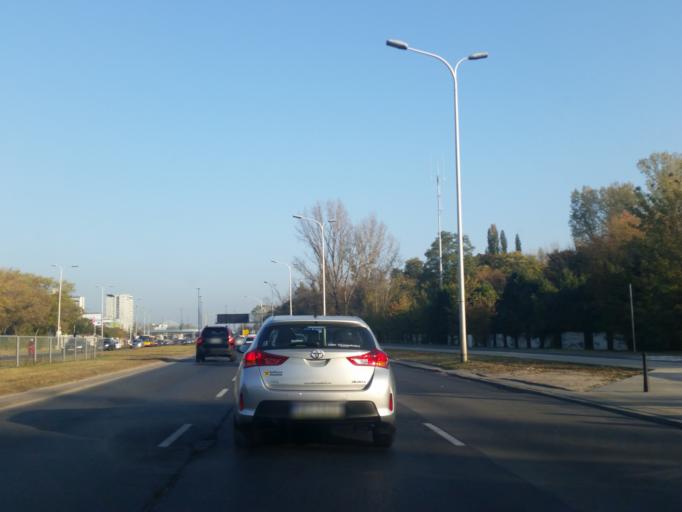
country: PL
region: Masovian Voivodeship
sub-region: Warszawa
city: Mokotow
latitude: 52.2187
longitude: 21.0459
